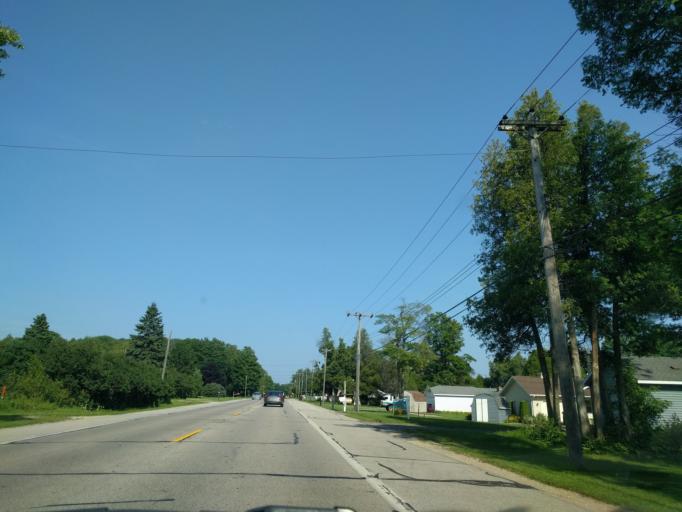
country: US
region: Michigan
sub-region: Delta County
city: Escanaba
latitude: 45.6865
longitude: -87.1129
